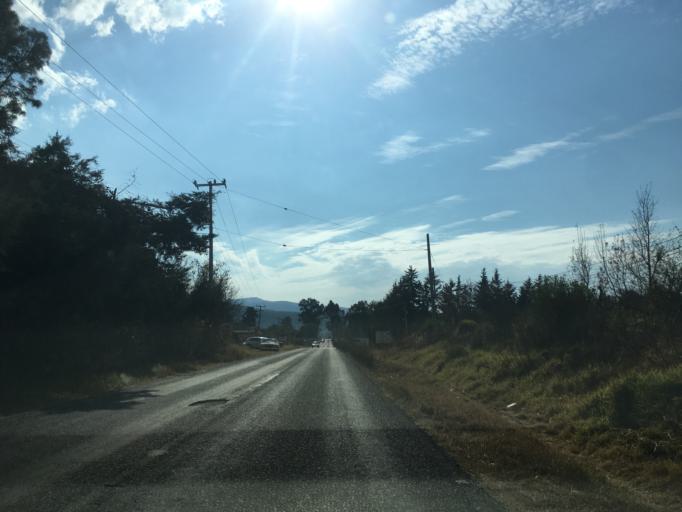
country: MX
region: Michoacan
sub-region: Patzcuaro
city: Santa Ana Chapitiro
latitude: 19.5373
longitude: -101.6372
